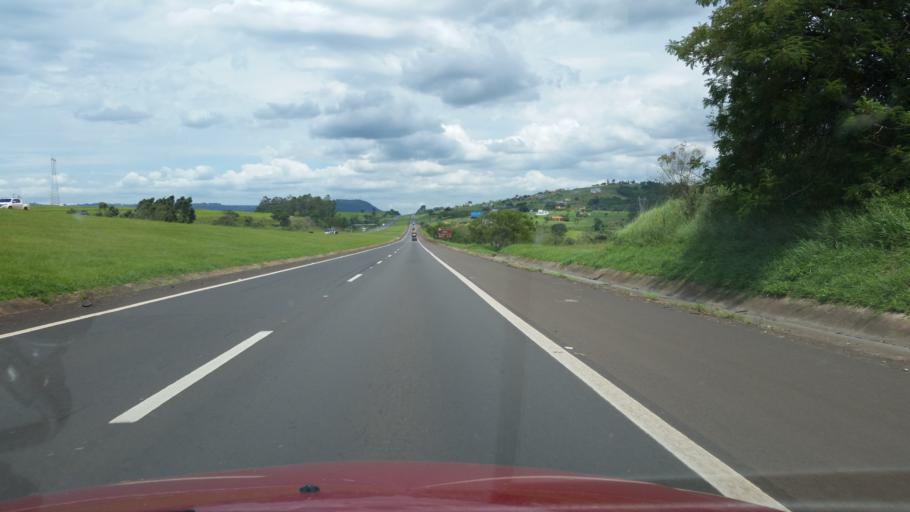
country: BR
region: Sao Paulo
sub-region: Itatinga
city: Itatinga
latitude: -23.1392
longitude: -48.4381
